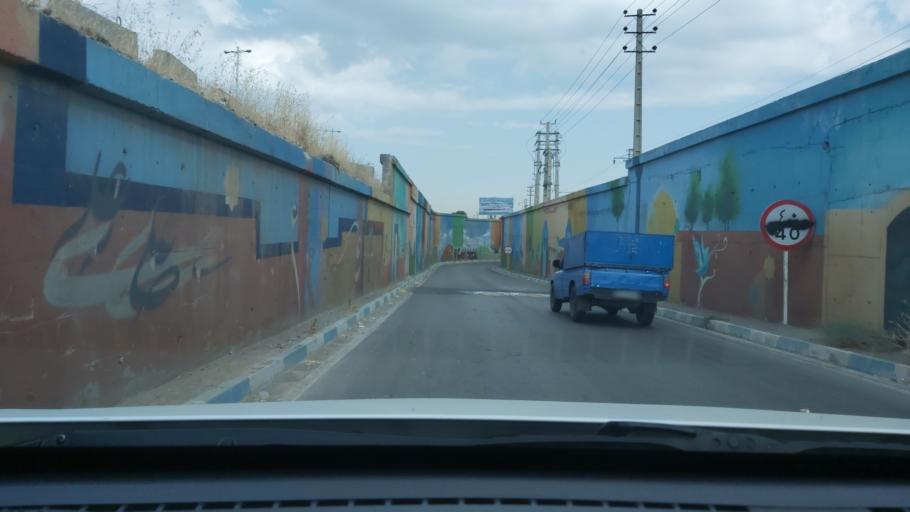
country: IR
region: Alborz
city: Hashtgerd
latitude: 35.9340
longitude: 50.7577
